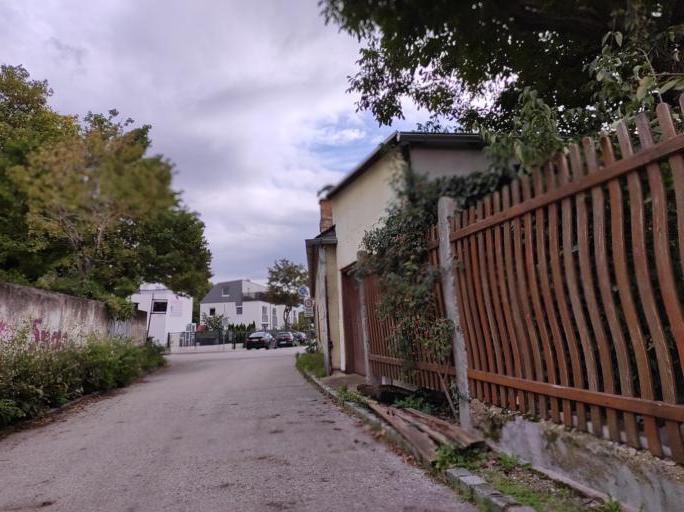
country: AT
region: Lower Austria
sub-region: Politischer Bezirk Baden
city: Baden
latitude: 48.0039
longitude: 16.2508
